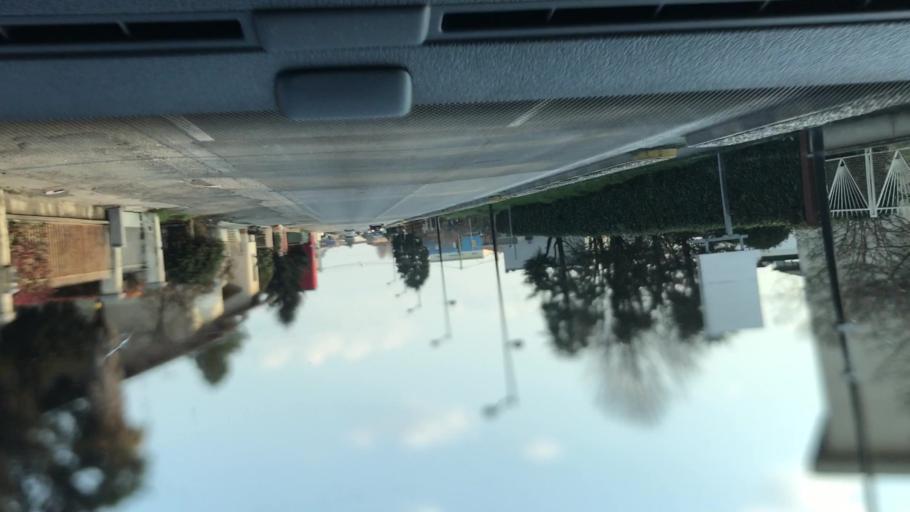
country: IT
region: Emilia-Romagna
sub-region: Provincia di Parma
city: Mezzano Inferiore
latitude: 44.9447
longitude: 10.4769
